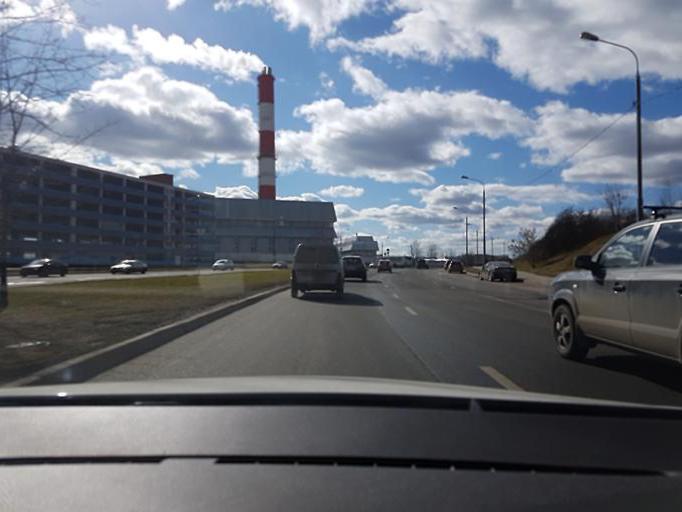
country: RU
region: Moskovskaya
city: Pavshino
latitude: 55.8406
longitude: 37.3506
